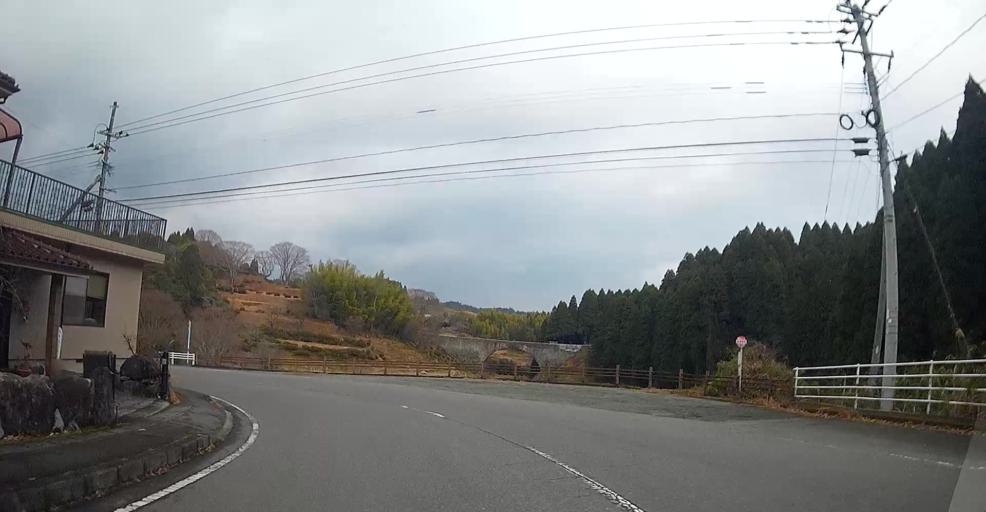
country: JP
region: Kumamoto
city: Ozu
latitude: 32.6810
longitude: 130.9912
